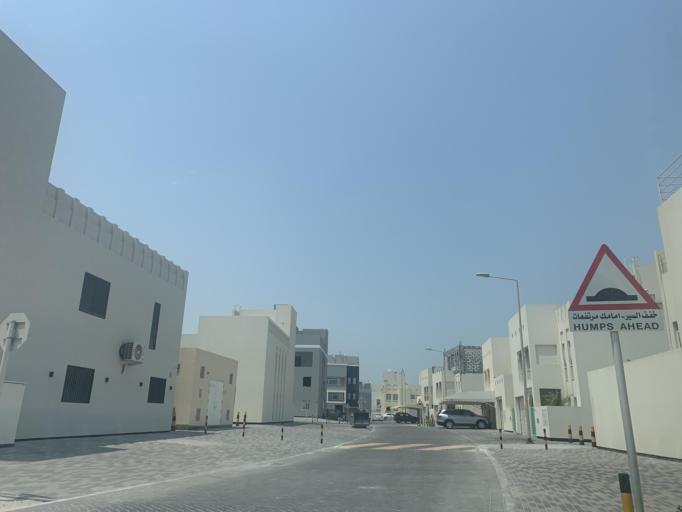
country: BH
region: Muharraq
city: Al Hadd
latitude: 26.2315
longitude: 50.6618
